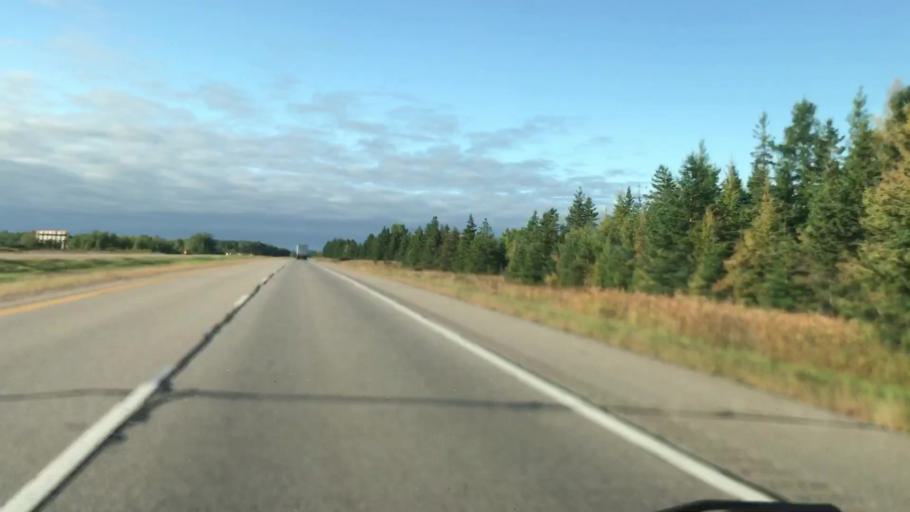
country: US
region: Michigan
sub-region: Chippewa County
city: Sault Ste. Marie
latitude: 46.4006
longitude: -84.4029
